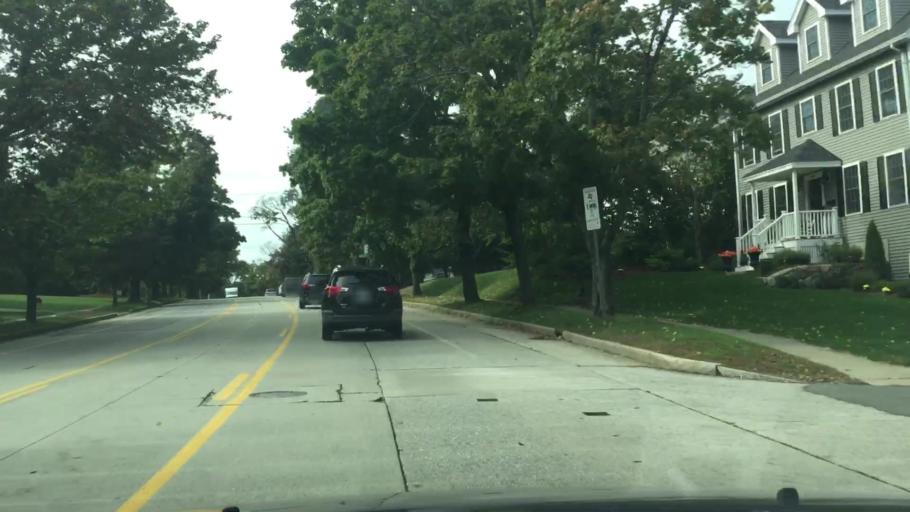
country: US
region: Massachusetts
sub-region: Middlesex County
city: Dracut
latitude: 42.6463
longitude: -71.2742
